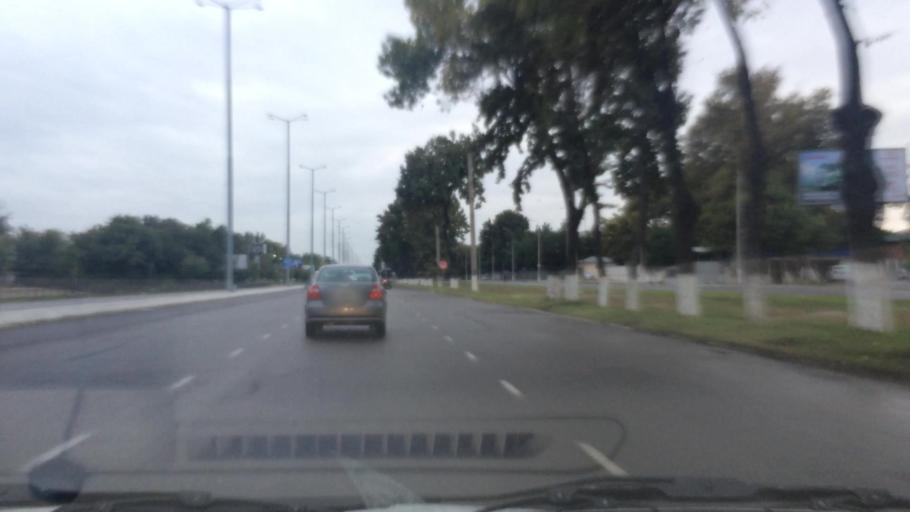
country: UZ
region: Toshkent Shahri
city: Tashkent
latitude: 41.2555
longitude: 69.1914
